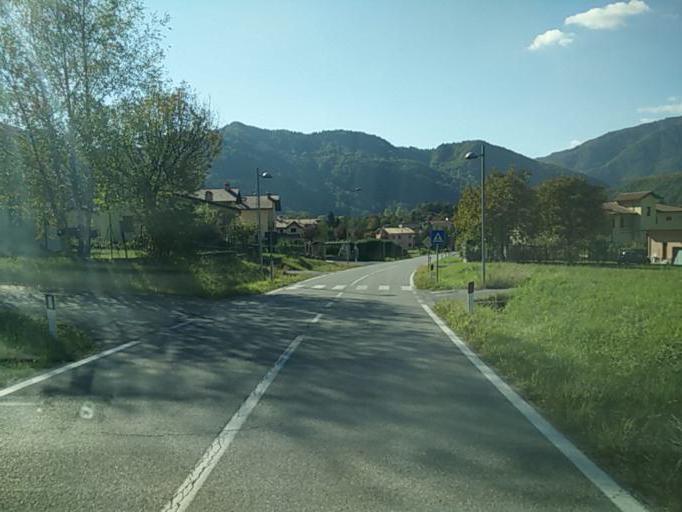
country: IT
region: Lombardy
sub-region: Provincia di Brescia
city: Crone
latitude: 45.7354
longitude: 10.4755
